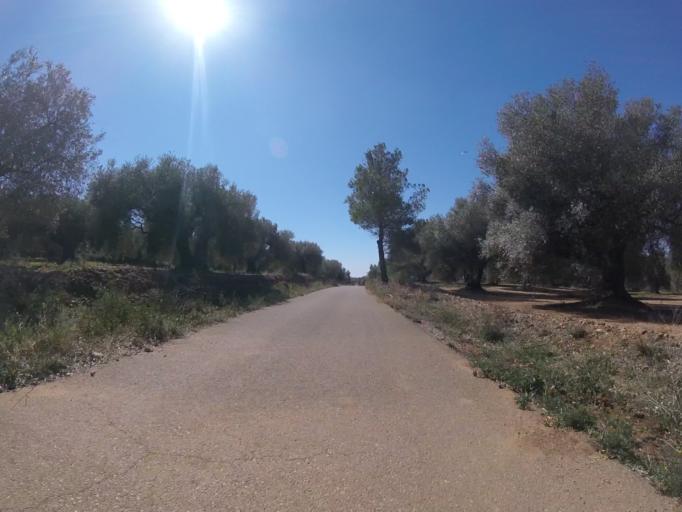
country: ES
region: Valencia
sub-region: Provincia de Castello
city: Cuevas de Vinroma
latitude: 40.3902
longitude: 0.1606
